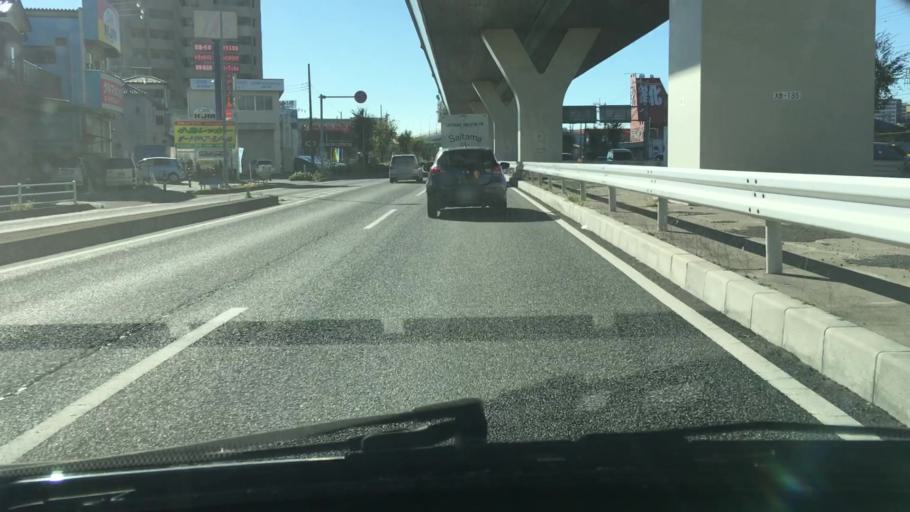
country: JP
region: Saitama
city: Yono
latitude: 35.8660
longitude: 139.6206
